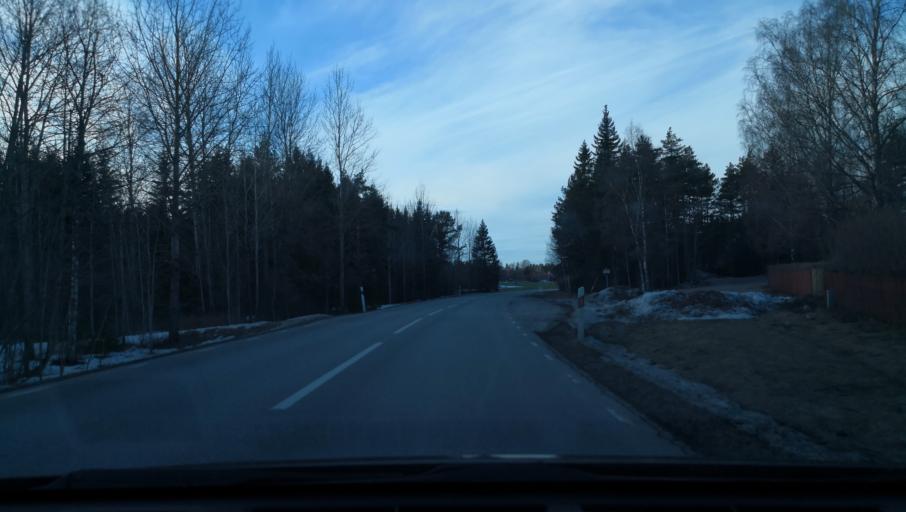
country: SE
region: Uppsala
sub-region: Osthammars Kommun
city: OEsthammar
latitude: 60.3004
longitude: 18.2776
